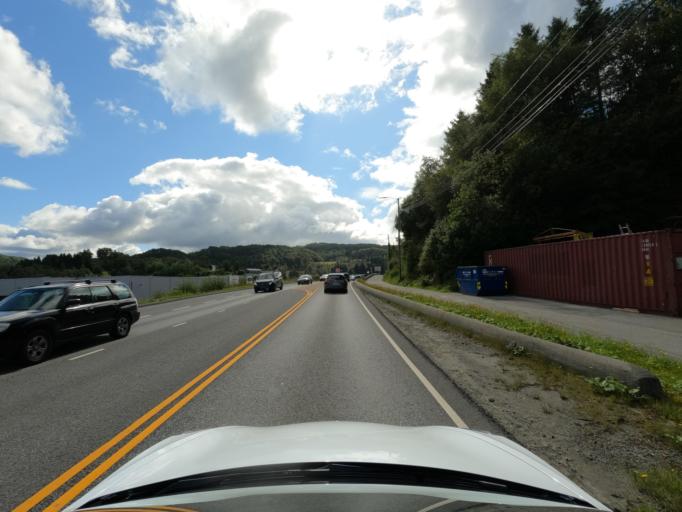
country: NO
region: Hordaland
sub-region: Bergen
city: Hylkje
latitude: 60.4862
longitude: 5.3763
